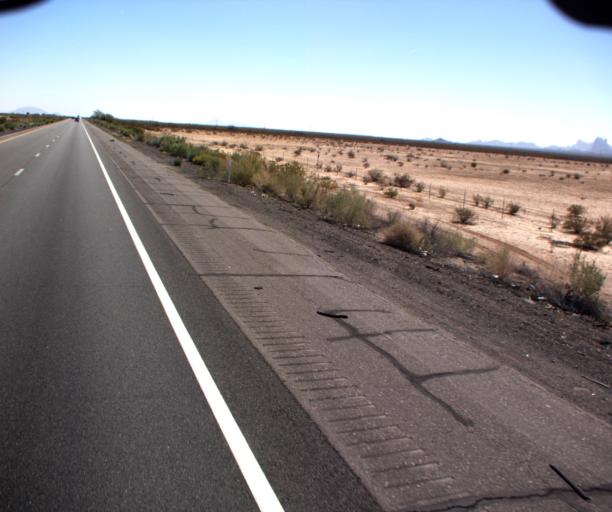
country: US
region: Arizona
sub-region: La Paz County
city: Salome
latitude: 33.5842
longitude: -113.4557
